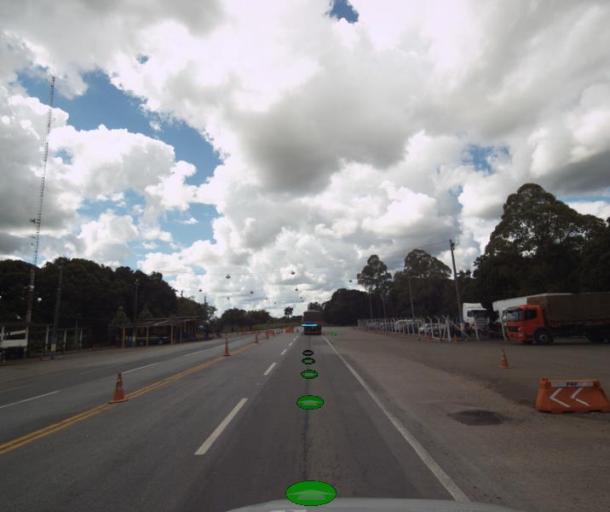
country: BR
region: Goias
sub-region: Porangatu
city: Porangatu
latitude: -13.4069
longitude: -49.1312
